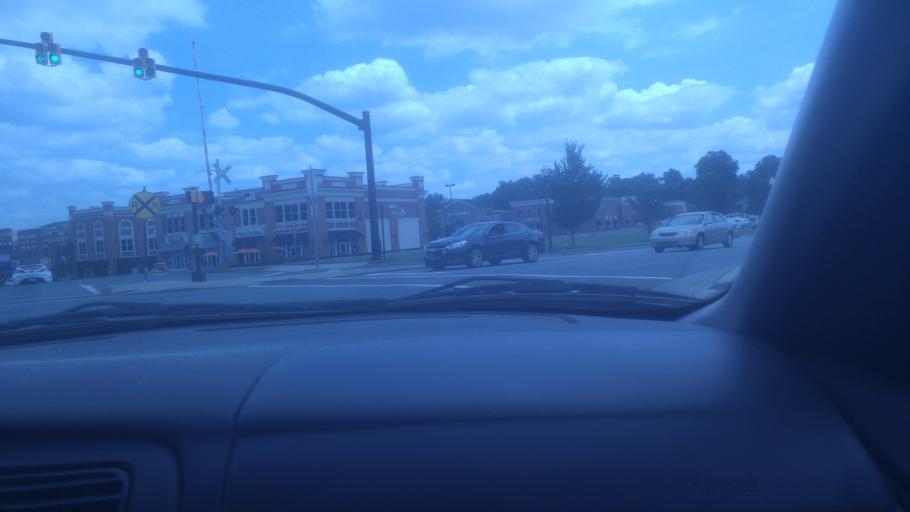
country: US
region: North Carolina
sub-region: Mecklenburg County
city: Cornelius
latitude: 35.4812
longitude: -80.8580
